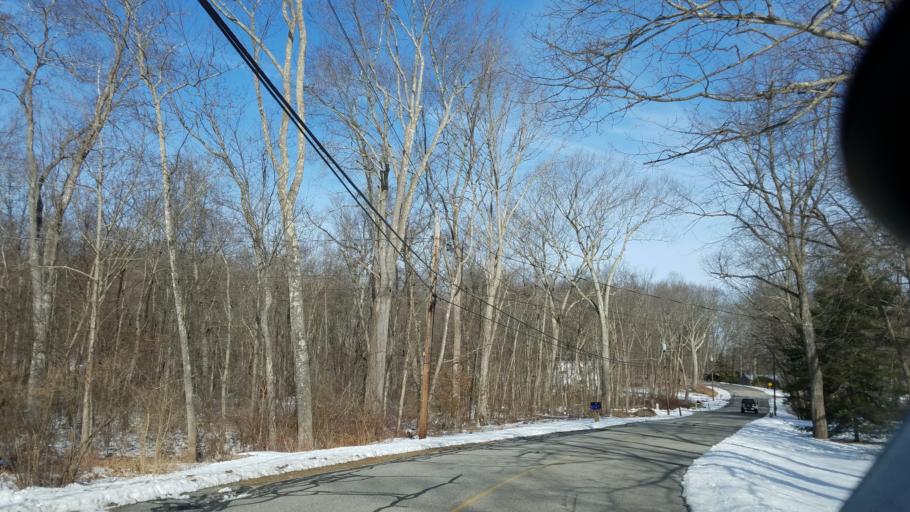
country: US
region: Connecticut
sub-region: Tolland County
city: Coventry Lake
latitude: 41.7217
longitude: -72.3631
